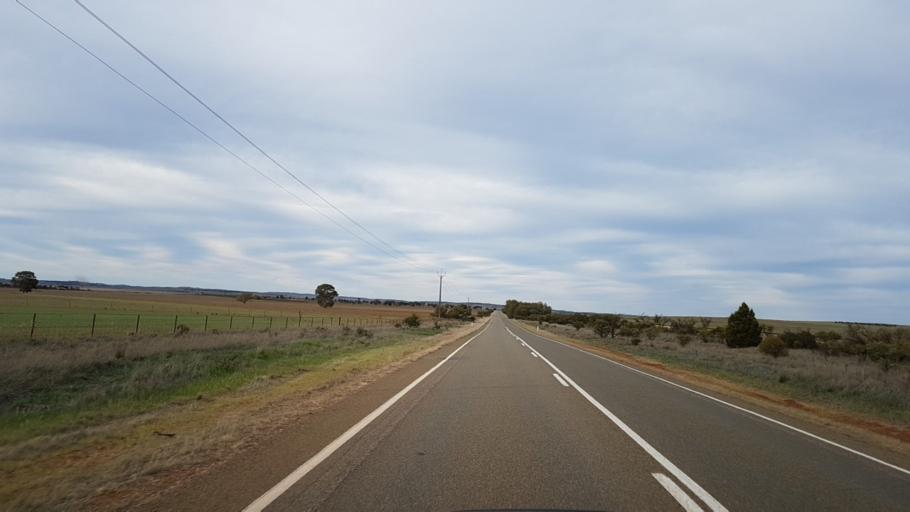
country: AU
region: South Australia
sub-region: Peterborough
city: Peterborough
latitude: -33.0005
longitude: 138.7779
